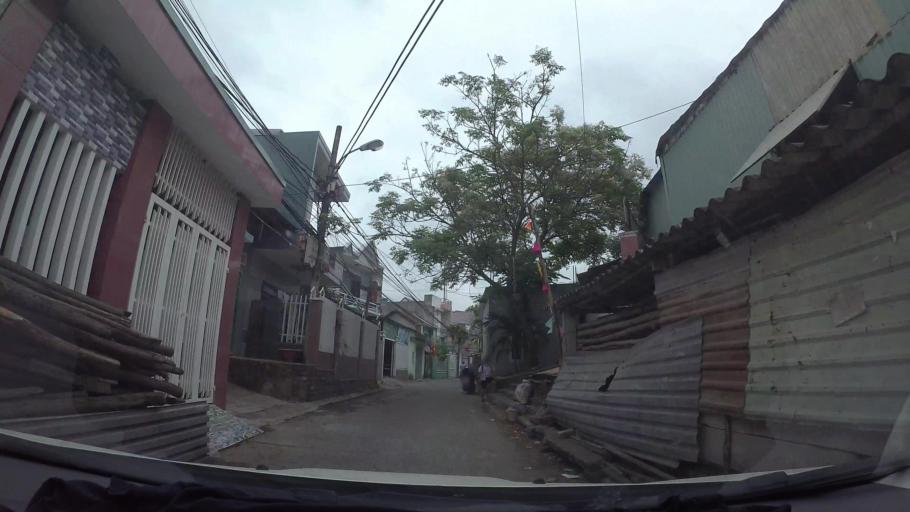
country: VN
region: Da Nang
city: Lien Chieu
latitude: 16.1053
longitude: 108.1317
